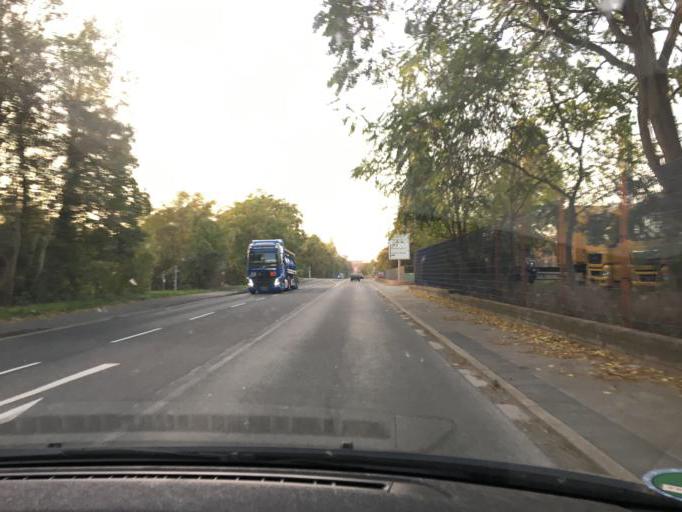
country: DE
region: North Rhine-Westphalia
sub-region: Regierungsbezirk Koln
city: Hurth
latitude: 50.8564
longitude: 6.8377
